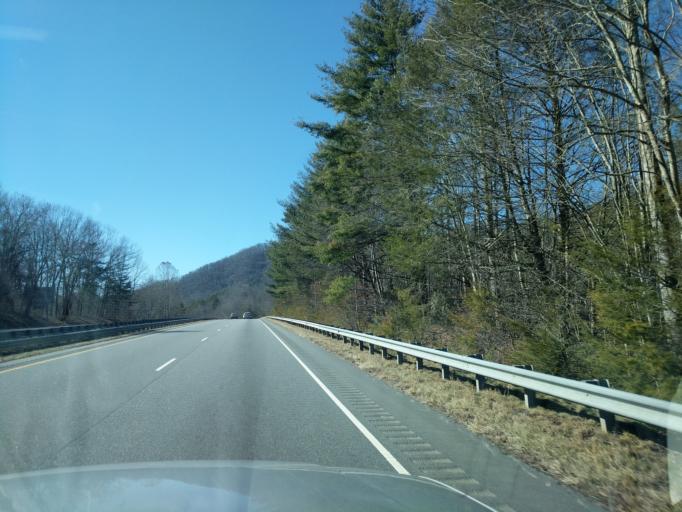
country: US
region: North Carolina
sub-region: Jackson County
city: Sylva
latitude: 35.3961
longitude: -83.2052
